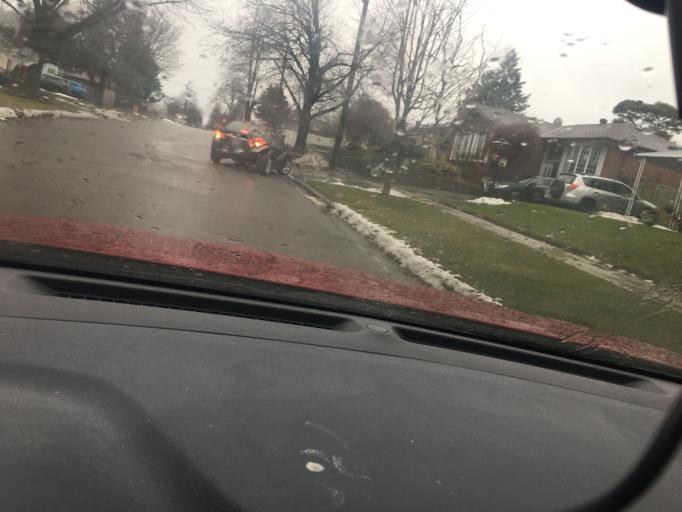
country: CA
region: Ontario
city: Scarborough
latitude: 43.7594
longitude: -79.2595
